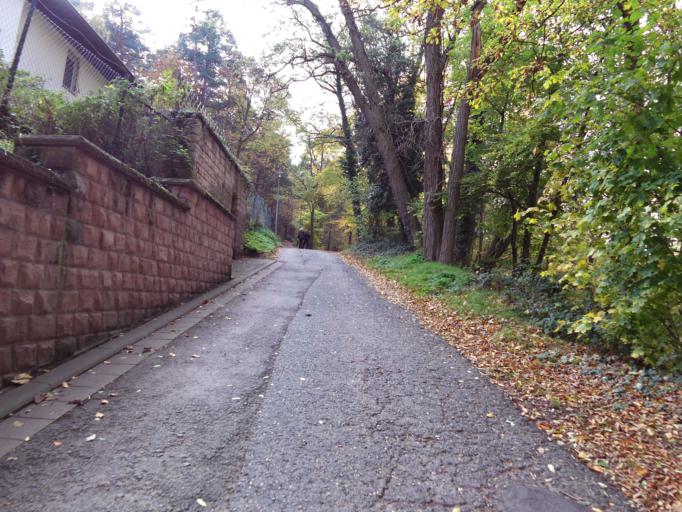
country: DE
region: Rheinland-Pfalz
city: Wachenheim
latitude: 49.4347
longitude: 8.1673
